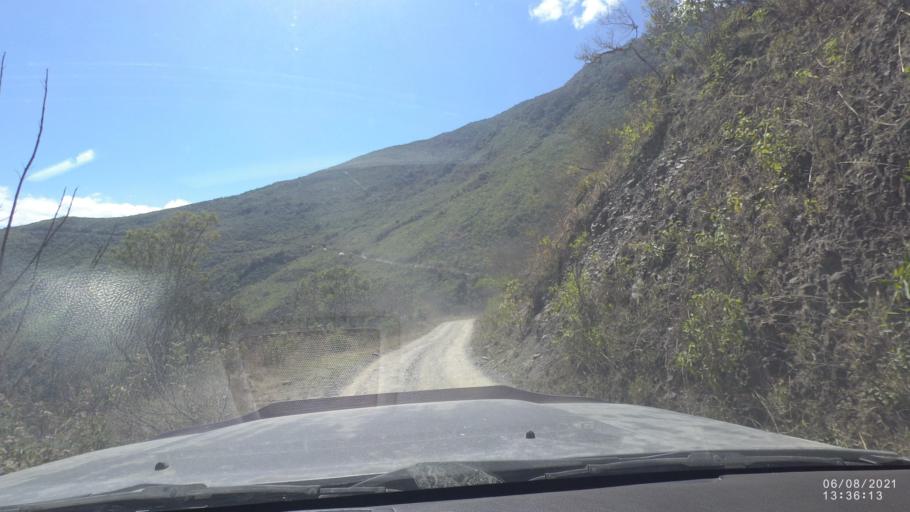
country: BO
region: La Paz
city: Quime
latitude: -16.6919
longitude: -66.7234
